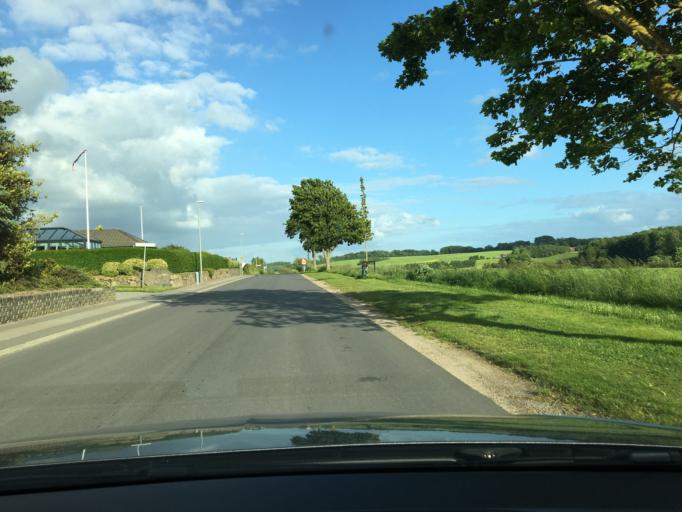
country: DK
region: Central Jutland
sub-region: Favrskov Kommune
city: Hadsten
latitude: 56.3073
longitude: 10.0958
